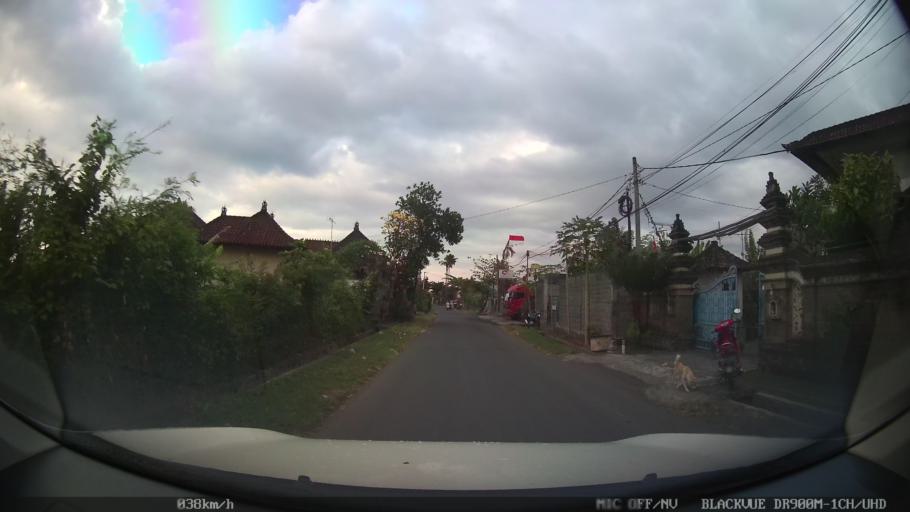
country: ID
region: Bali
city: Banjar Pasekan
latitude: -8.6387
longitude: 115.2823
